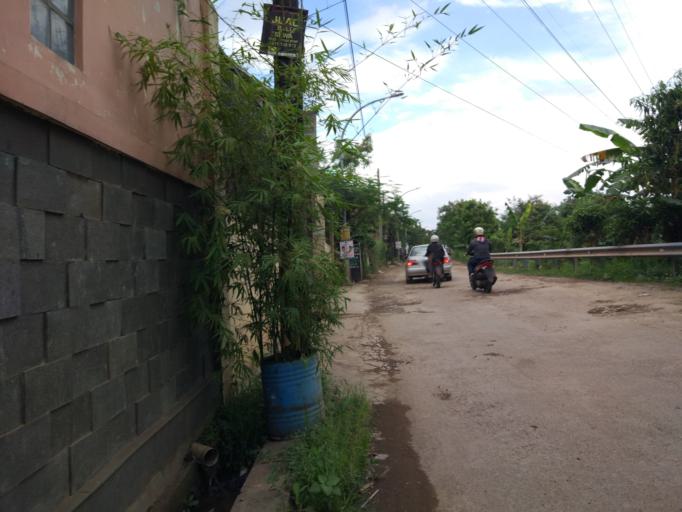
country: ID
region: West Java
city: Bandung
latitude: -6.9232
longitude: 107.6693
